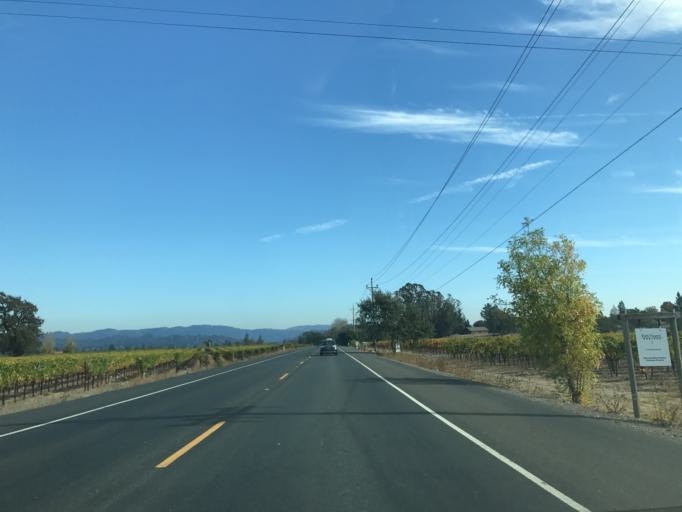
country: US
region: California
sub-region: Sonoma County
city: Larkfield-Wikiup
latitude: 38.4904
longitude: -122.7991
